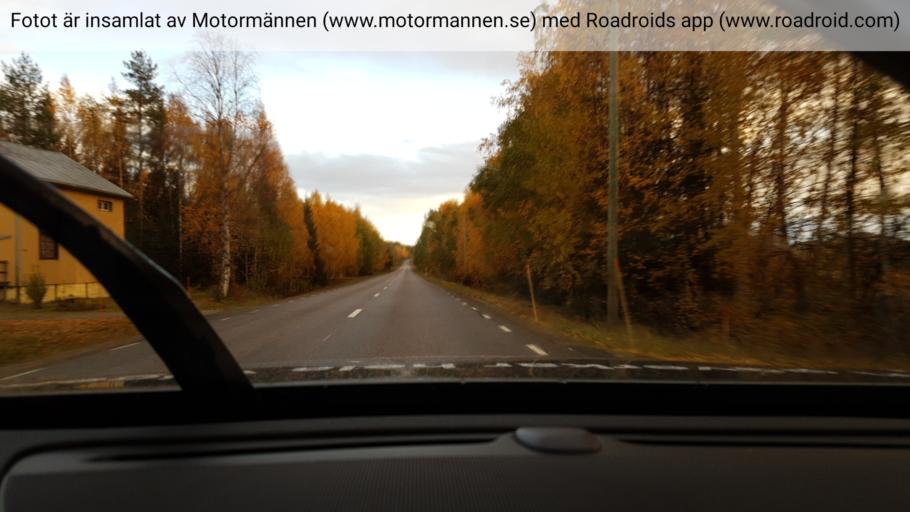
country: SE
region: Norrbotten
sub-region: Overkalix Kommun
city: OEverkalix
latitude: 66.5025
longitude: 22.7669
